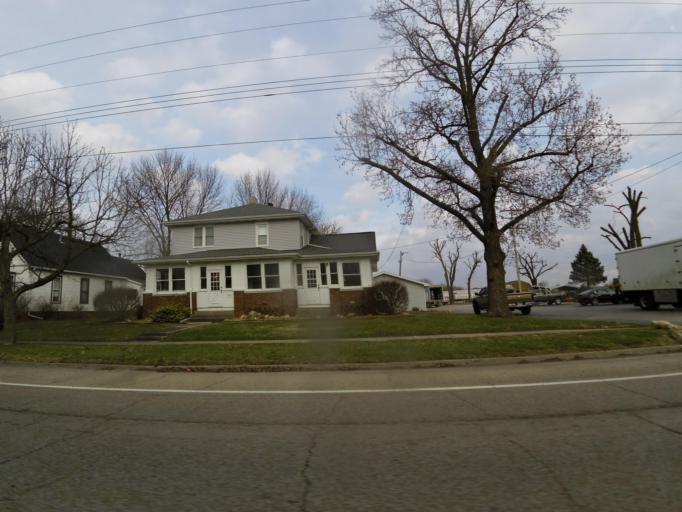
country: US
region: Illinois
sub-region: Christian County
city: Pana
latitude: 39.3895
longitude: -89.0751
